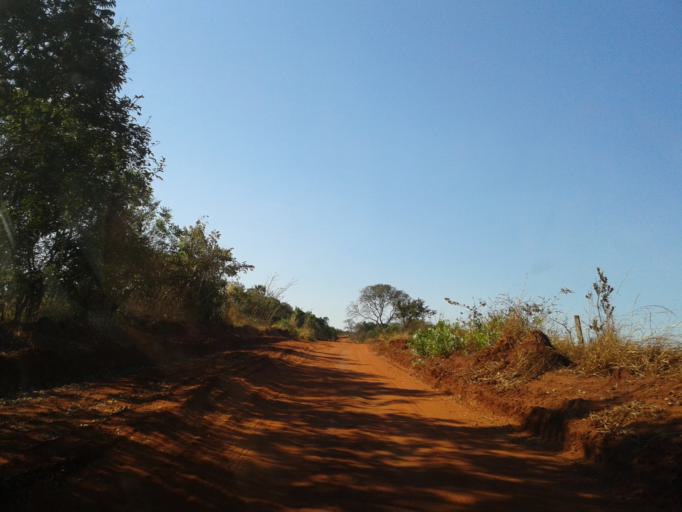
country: BR
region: Minas Gerais
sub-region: Ituiutaba
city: Ituiutaba
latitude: -19.0034
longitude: -49.3685
